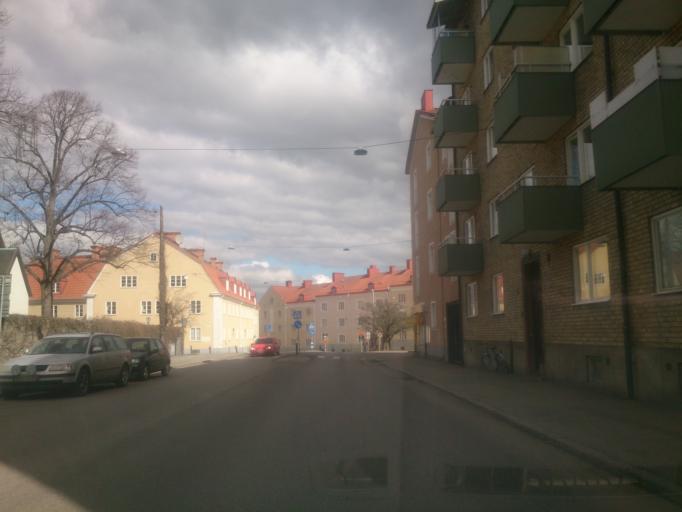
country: SE
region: OEstergoetland
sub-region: Norrkopings Kommun
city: Norrkoping
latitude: 58.5826
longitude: 16.1857
